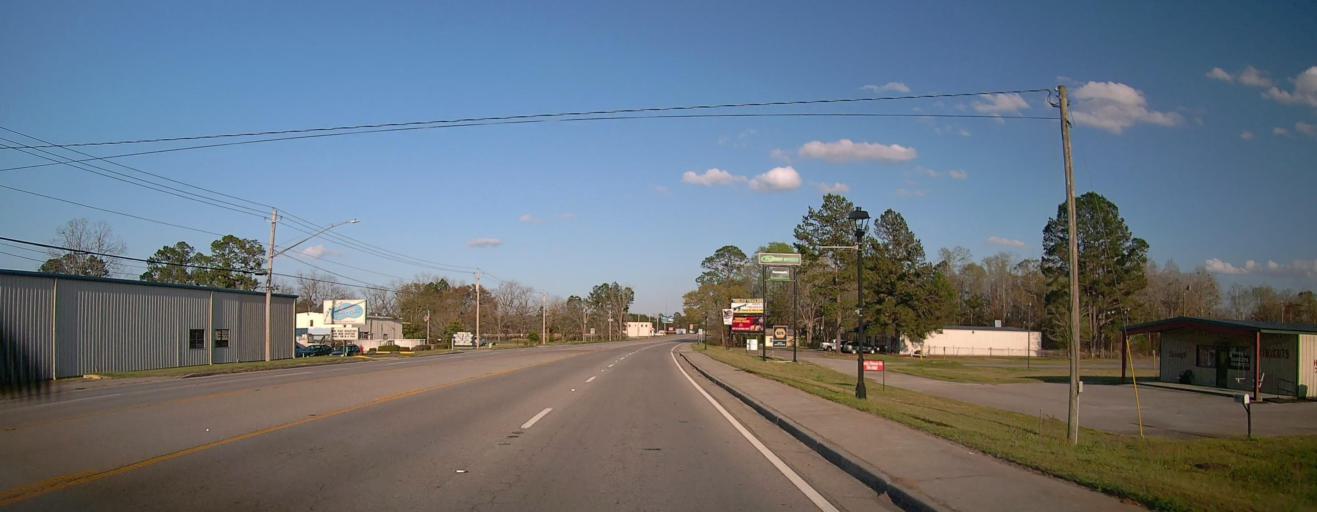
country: US
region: Georgia
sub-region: Evans County
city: Claxton
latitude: 32.1597
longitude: -81.9299
